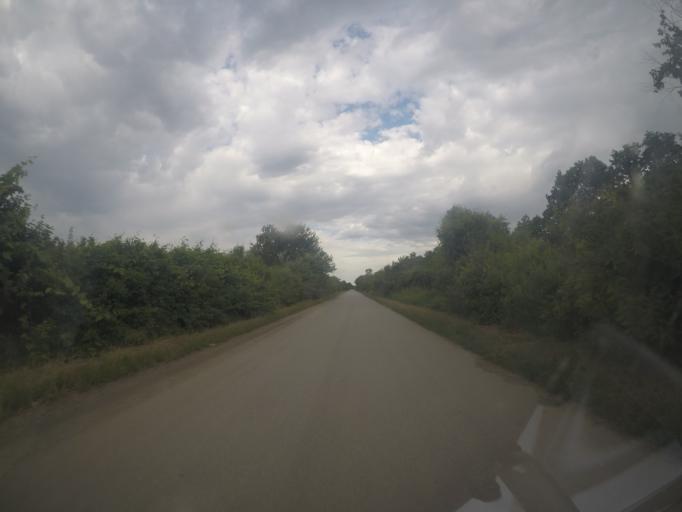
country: RS
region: Central Serbia
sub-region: Belgrade
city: Zemun
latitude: 44.8987
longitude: 20.4090
